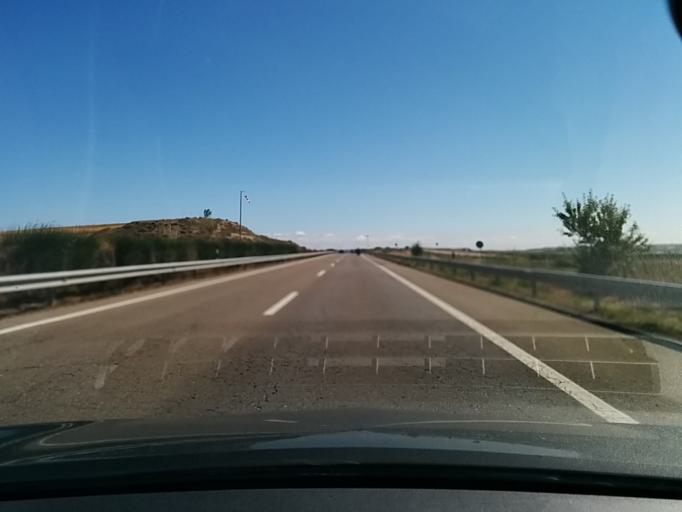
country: ES
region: Aragon
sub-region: Provincia de Huesca
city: Almudebar
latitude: 42.0124
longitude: -0.6242
